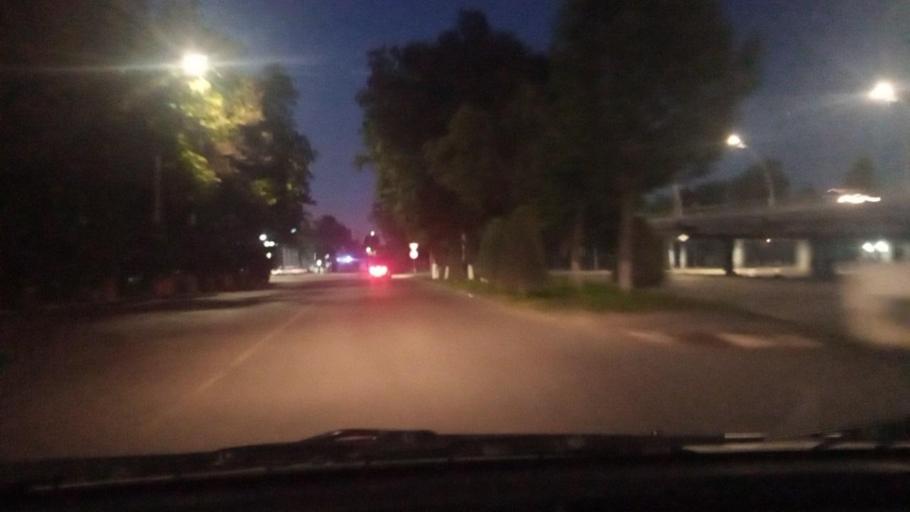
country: UZ
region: Toshkent Shahri
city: Tashkent
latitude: 41.2702
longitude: 69.2610
